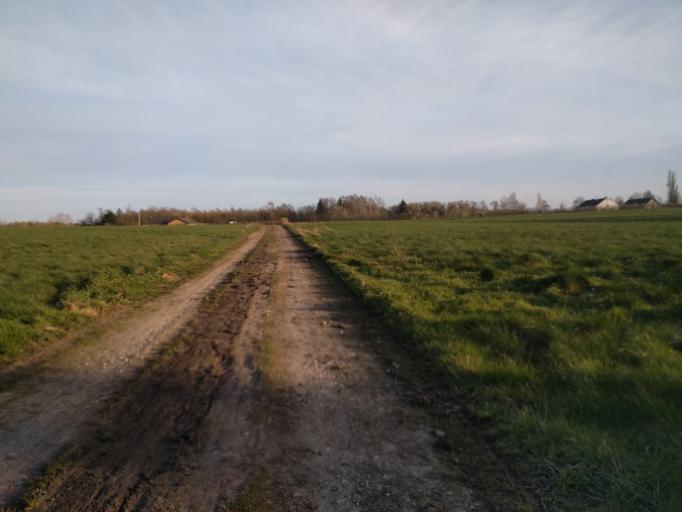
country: DK
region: South Denmark
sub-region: Kerteminde Kommune
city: Langeskov
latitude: 55.3766
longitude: 10.5738
